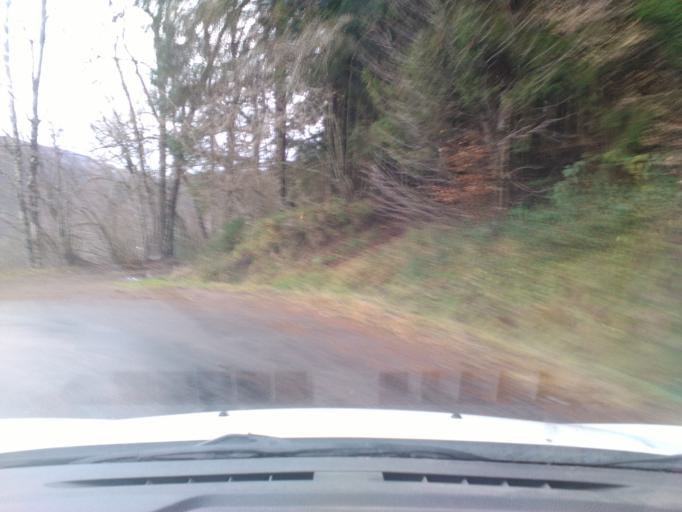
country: FR
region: Lorraine
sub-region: Departement des Vosges
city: La Bresse
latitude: 47.9735
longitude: 6.8564
